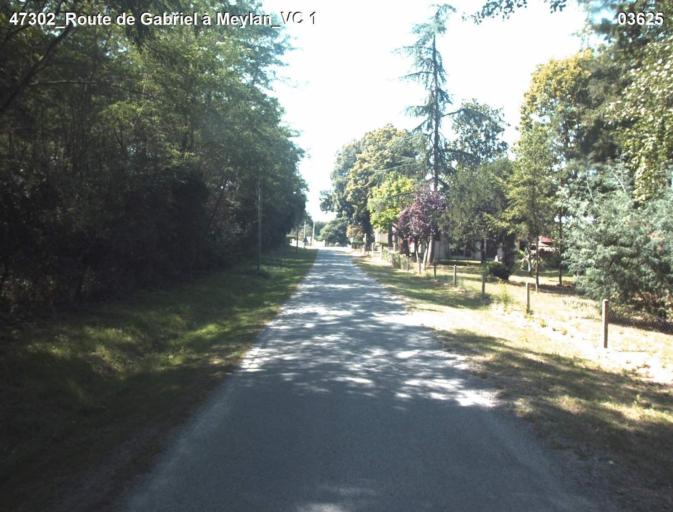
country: FR
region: Aquitaine
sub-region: Departement du Lot-et-Garonne
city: Mezin
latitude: 44.0751
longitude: 0.1208
